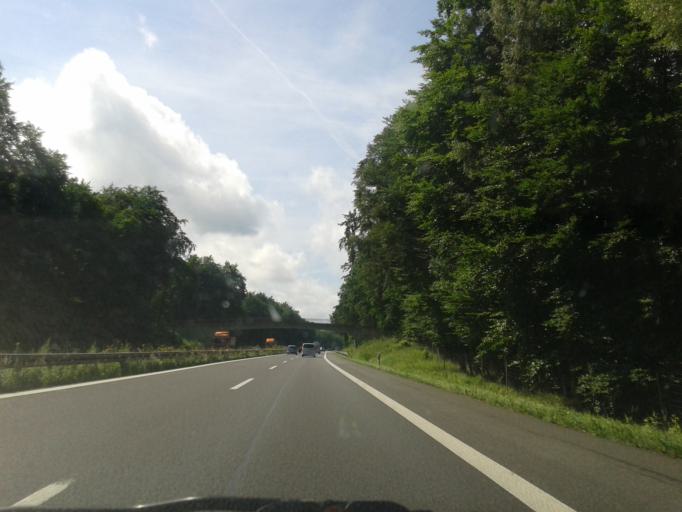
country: DE
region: Brandenburg
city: Gramzow
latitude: 53.1700
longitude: 13.9196
